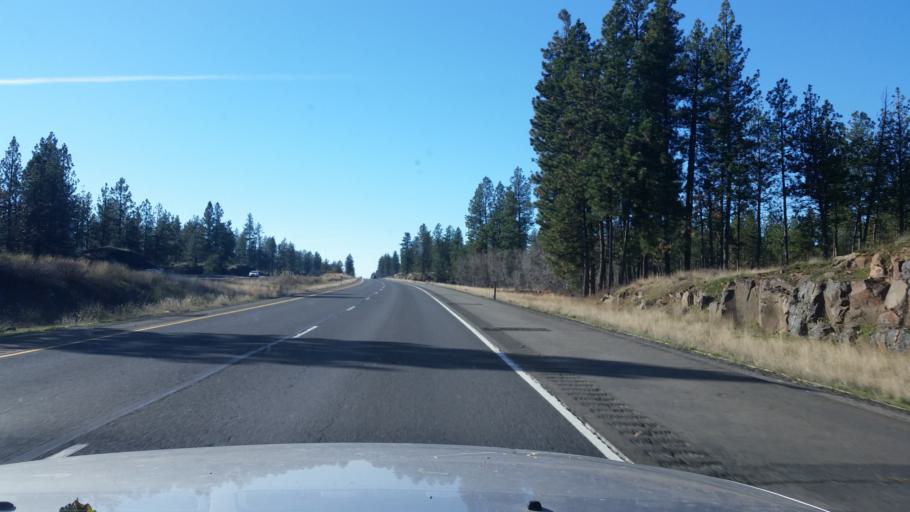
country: US
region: Washington
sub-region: Spokane County
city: Medical Lake
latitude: 47.5276
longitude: -117.6597
